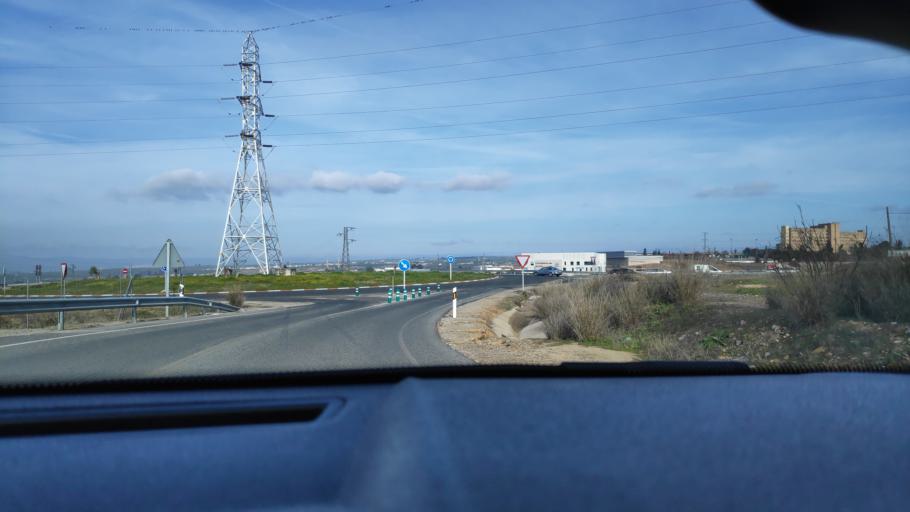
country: ES
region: Andalusia
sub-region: Provincia de Jaen
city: Linares
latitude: 38.0813
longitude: -3.6440
